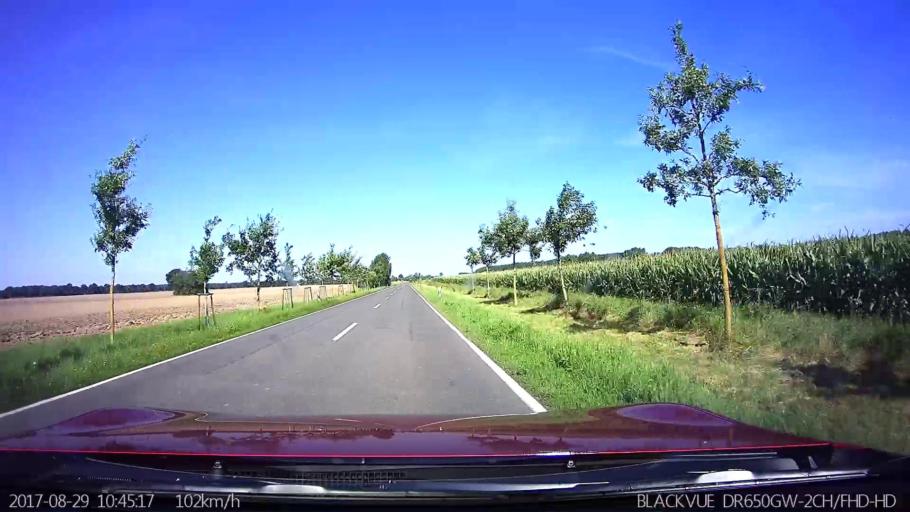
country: DE
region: Mecklenburg-Vorpommern
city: Richtenberg
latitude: 54.2115
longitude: 12.8652
